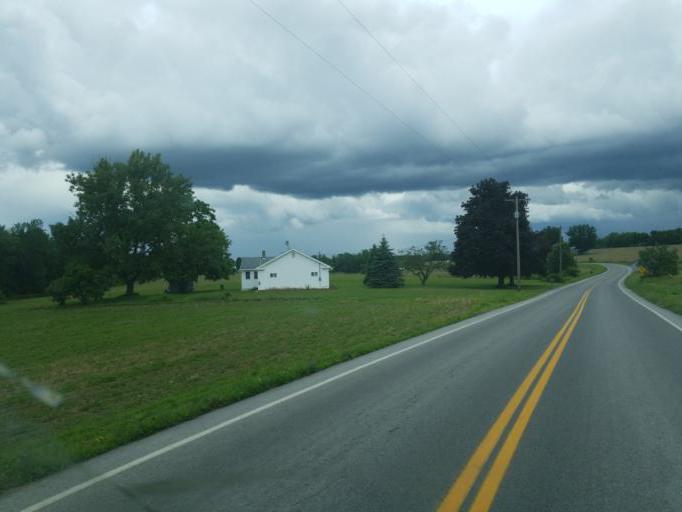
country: US
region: New York
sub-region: Wayne County
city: Clyde
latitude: 43.0347
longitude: -76.9071
